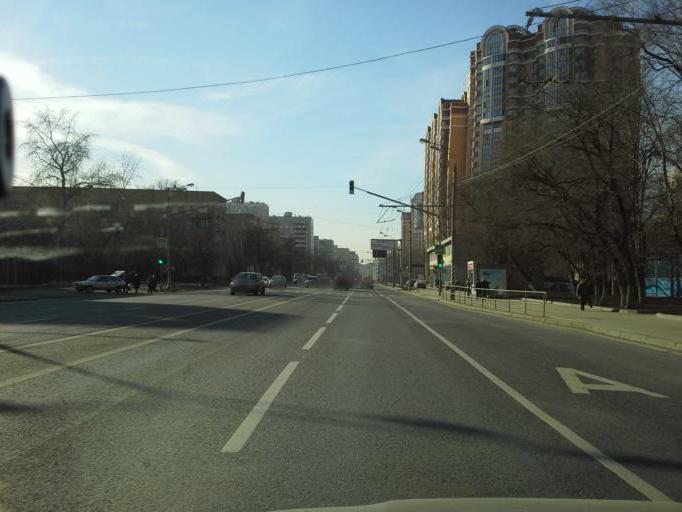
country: RU
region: Moscow
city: Taganskiy
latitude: 55.7374
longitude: 37.6888
